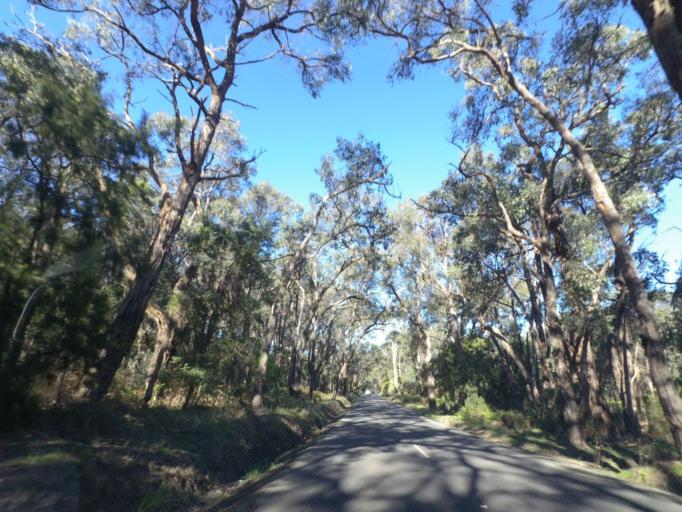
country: AU
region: Victoria
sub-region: Yarra Ranges
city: Montrose
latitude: -37.8018
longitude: 145.3424
